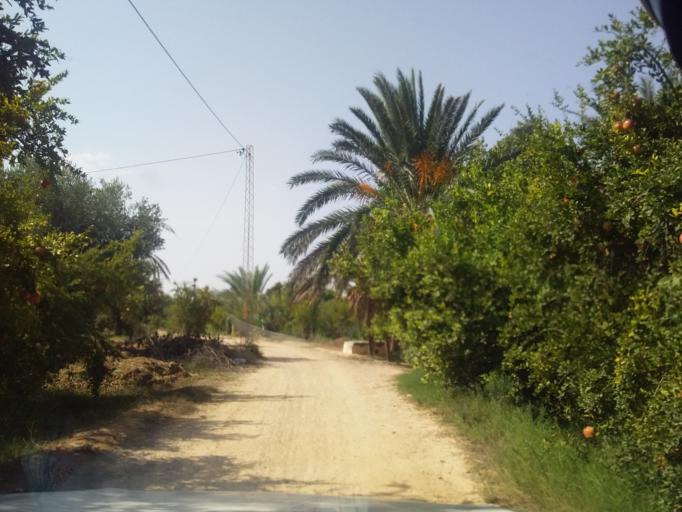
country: TN
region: Qabis
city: Gabes
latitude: 33.6274
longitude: 10.2913
